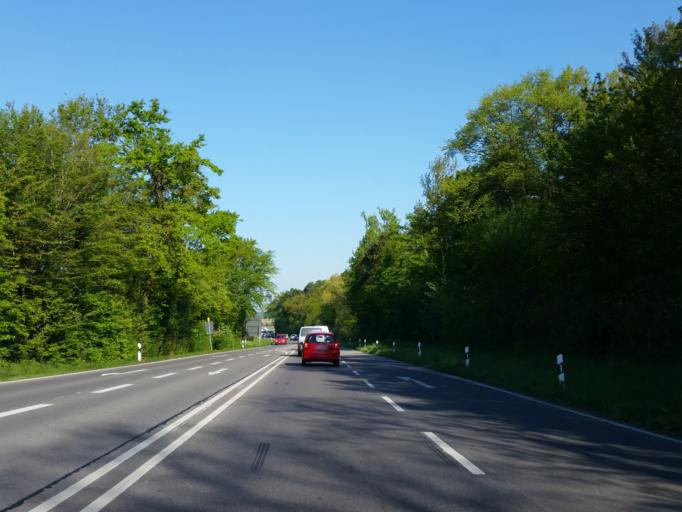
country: CH
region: Thurgau
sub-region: Kreuzlingen District
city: Ermatingen
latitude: 47.7015
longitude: 9.1123
